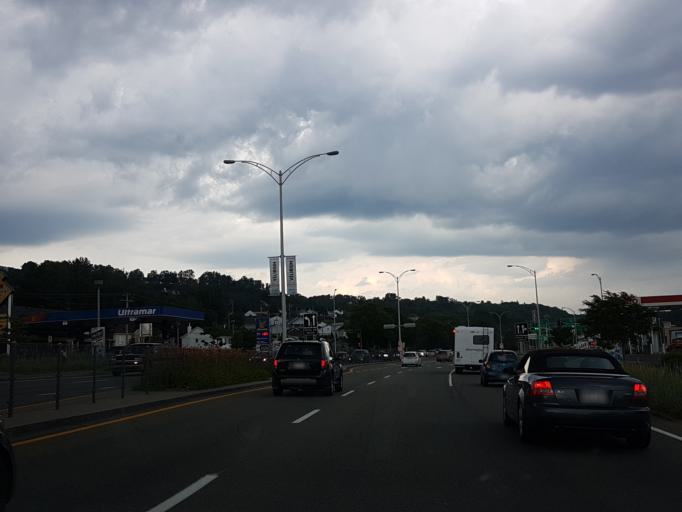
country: CA
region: Quebec
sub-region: Capitale-Nationale
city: Beaupre
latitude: 47.0418
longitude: -70.8970
